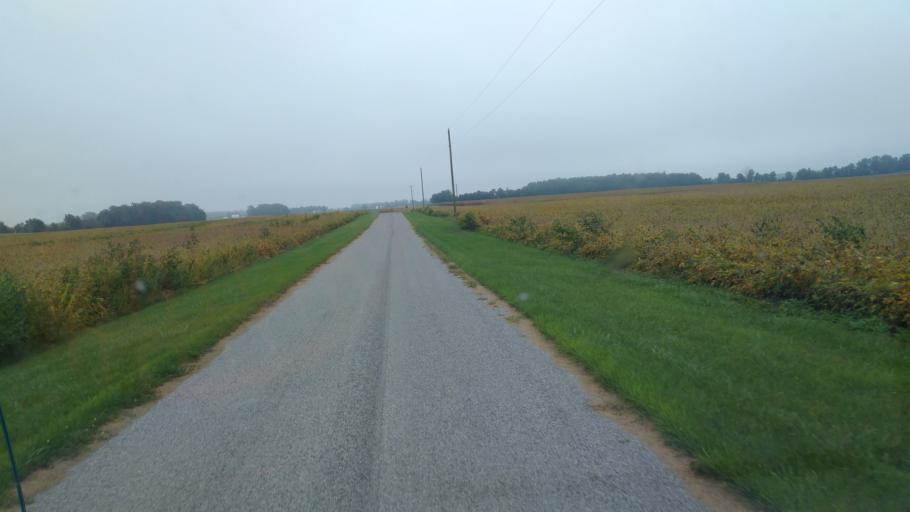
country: US
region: Ohio
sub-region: Union County
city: Richwood
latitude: 40.4976
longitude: -83.3641
